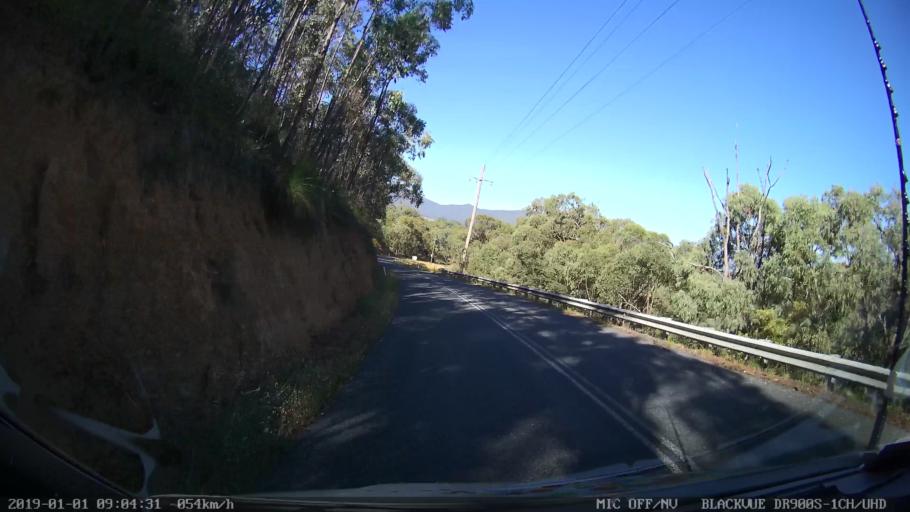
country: AU
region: New South Wales
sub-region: Snowy River
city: Jindabyne
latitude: -36.2206
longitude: 148.1554
